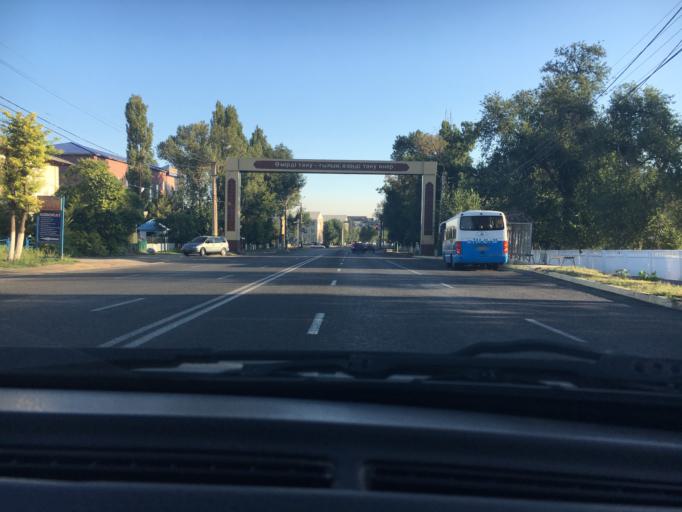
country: KZ
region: Zhambyl
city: Taraz
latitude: 42.8989
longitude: 71.3601
